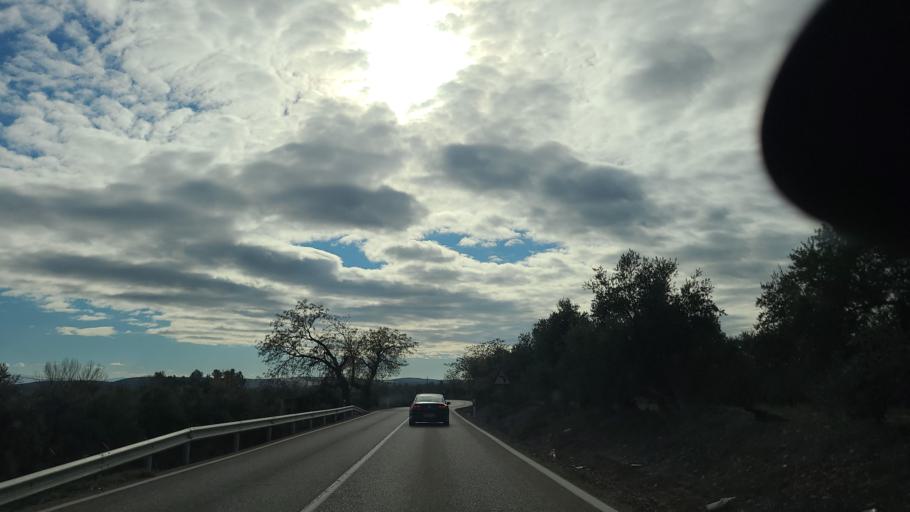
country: ES
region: Andalusia
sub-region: Provincia de Jaen
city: Villanueva de la Reina
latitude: 38.0333
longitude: -3.9171
